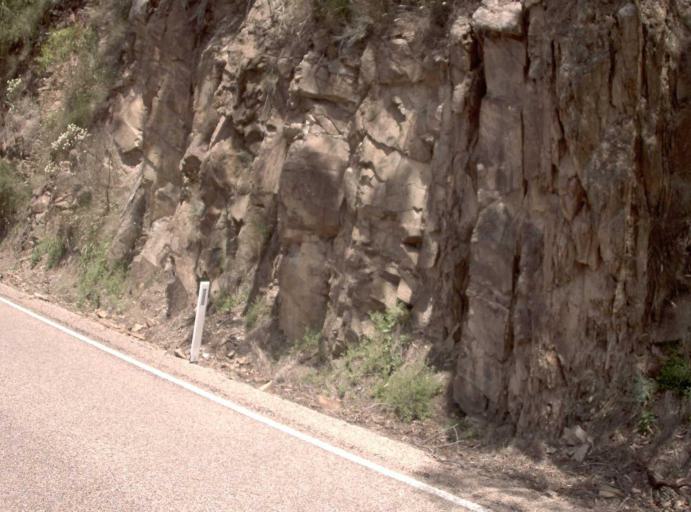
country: AU
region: Victoria
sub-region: East Gippsland
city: Lakes Entrance
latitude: -37.5485
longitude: 147.8668
